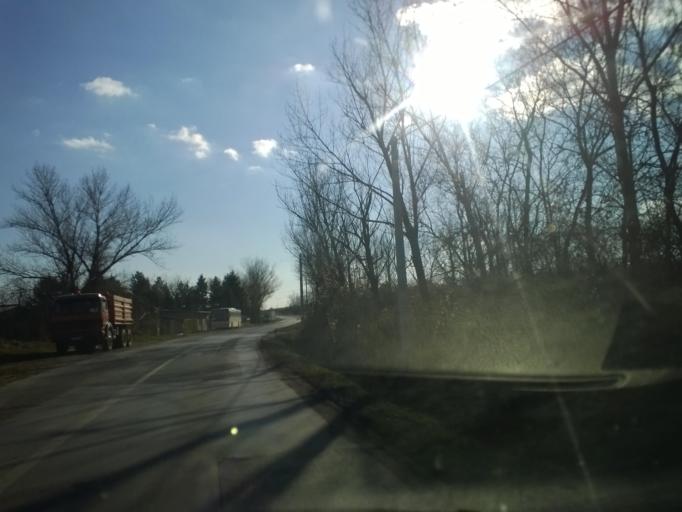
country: RS
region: Central Serbia
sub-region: Podunavski Okrug
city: Smederevo
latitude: 44.5854
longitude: 20.9755
